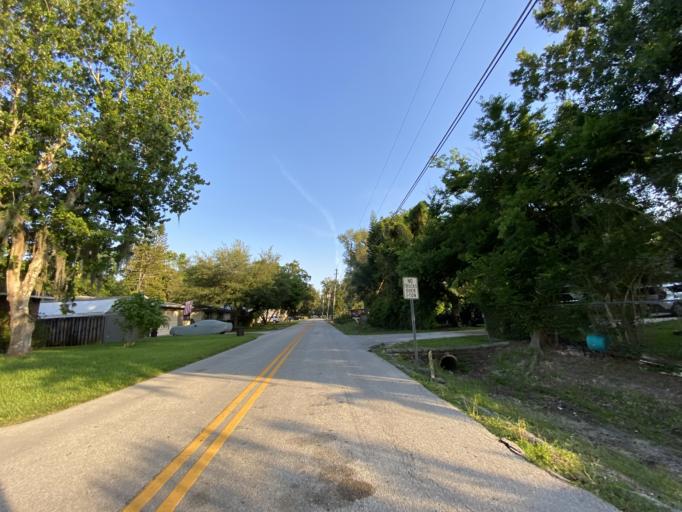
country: US
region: Florida
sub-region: Volusia County
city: Port Orange
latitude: 29.1344
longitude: -81.0065
